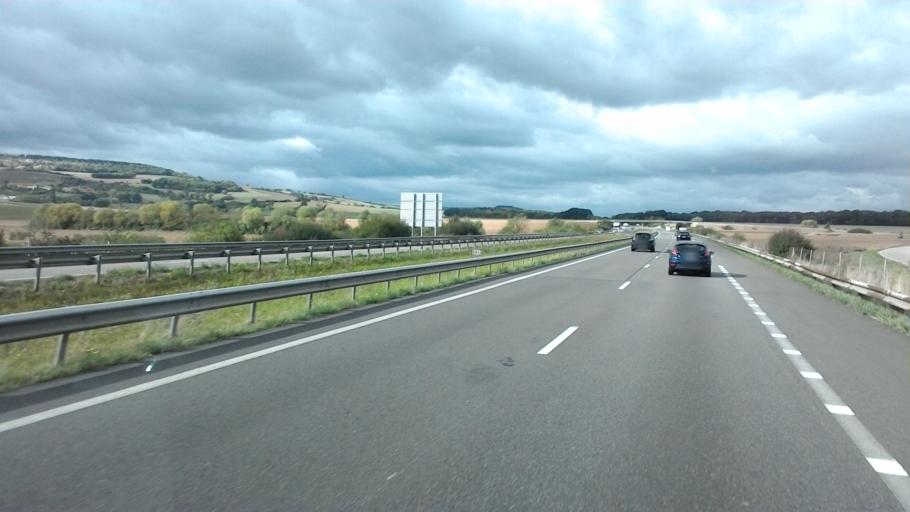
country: FR
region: Lorraine
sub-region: Departement de Meurthe-et-Moselle
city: Pont-a-Mousson
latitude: 48.9475
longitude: 6.1122
